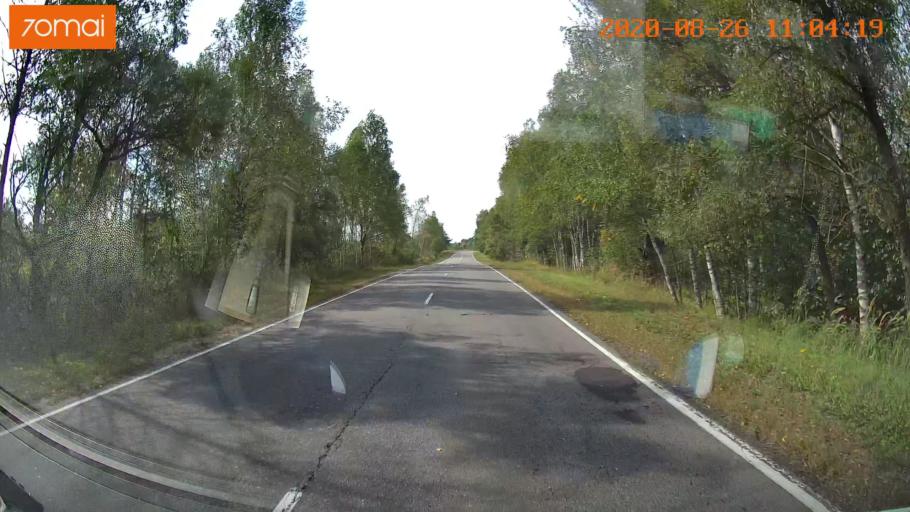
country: RU
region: Rjazan
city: Izhevskoye
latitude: 54.5310
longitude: 41.1973
